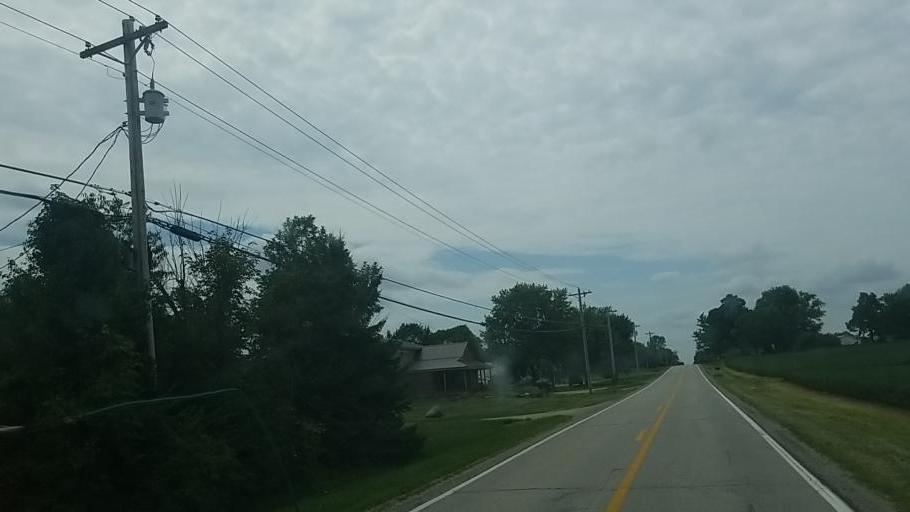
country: US
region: Ohio
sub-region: Franklin County
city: Groveport
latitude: 39.8274
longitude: -82.8803
